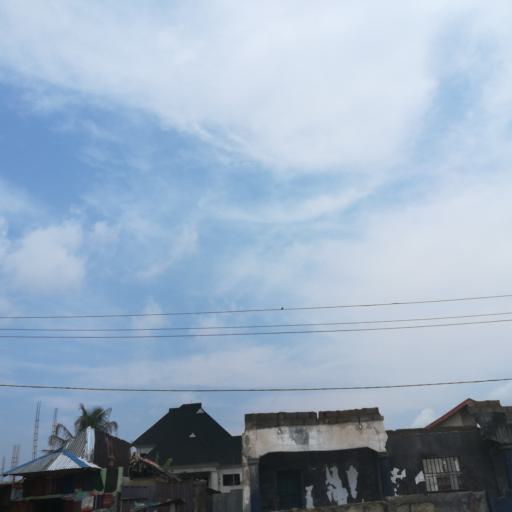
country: NG
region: Rivers
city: Port Harcourt
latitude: 4.8570
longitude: 7.0225
